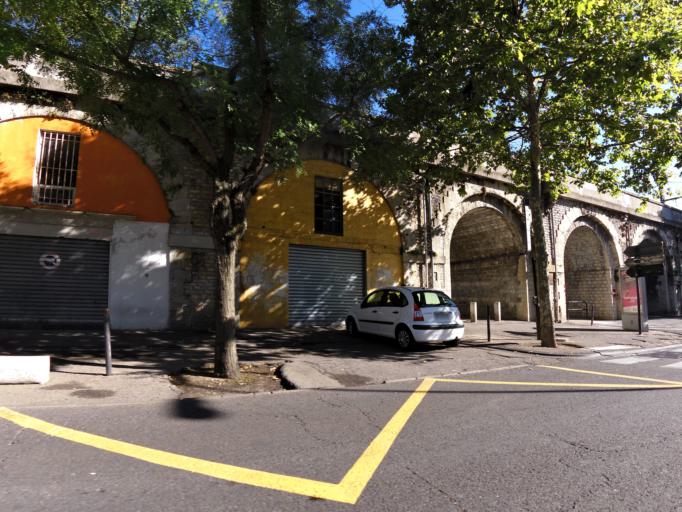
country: FR
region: Languedoc-Roussillon
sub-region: Departement du Gard
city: Nimes
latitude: 43.8355
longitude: 4.3695
